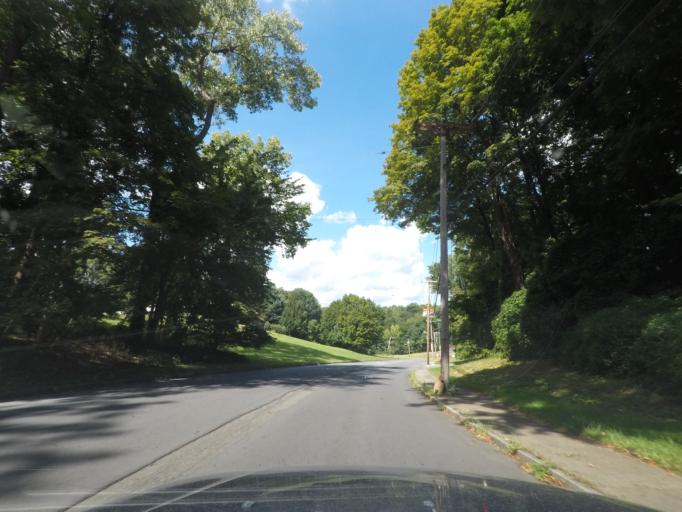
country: US
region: New York
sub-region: Rensselaer County
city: Troy
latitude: 42.7119
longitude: -73.6706
